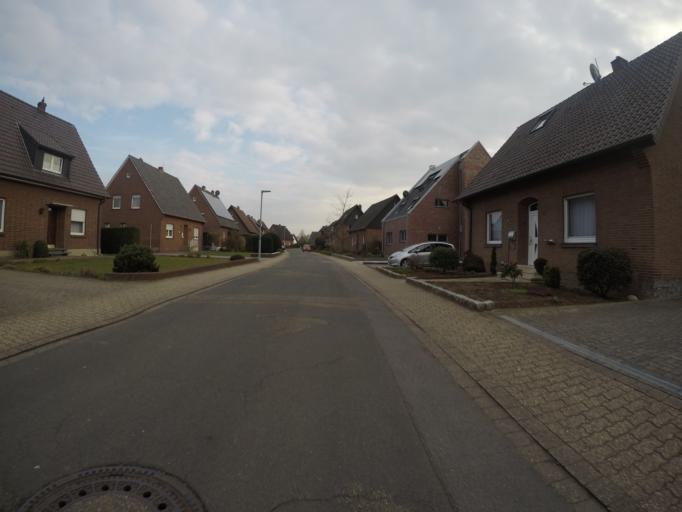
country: DE
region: North Rhine-Westphalia
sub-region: Regierungsbezirk Munster
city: Isselburg
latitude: 51.8205
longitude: 6.5168
